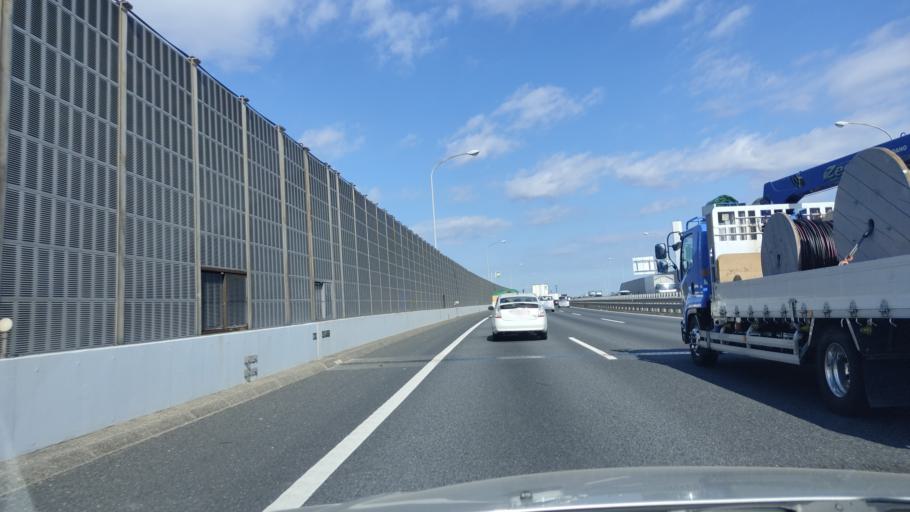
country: JP
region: Chiba
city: Nagareyama
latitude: 35.8705
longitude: 139.8827
